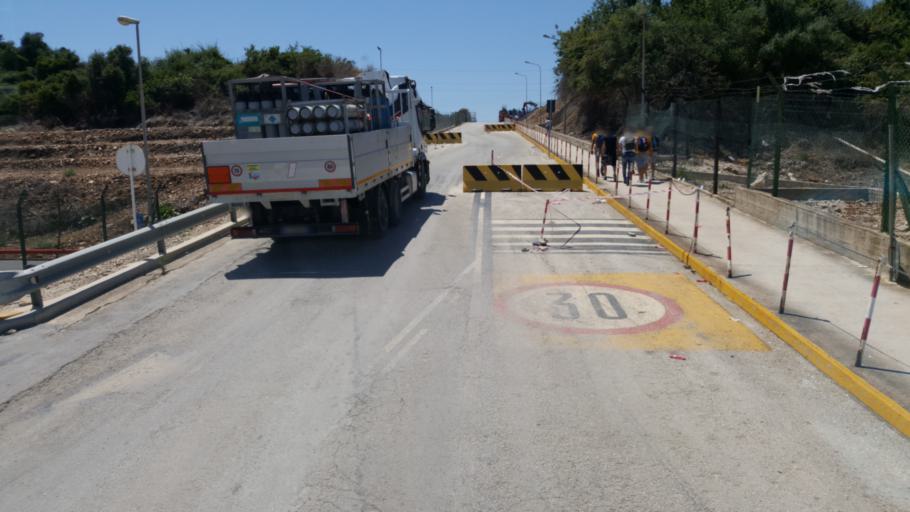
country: IT
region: Sicily
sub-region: Provincia di Siracusa
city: Melilli
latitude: 37.2074
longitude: 15.1665
